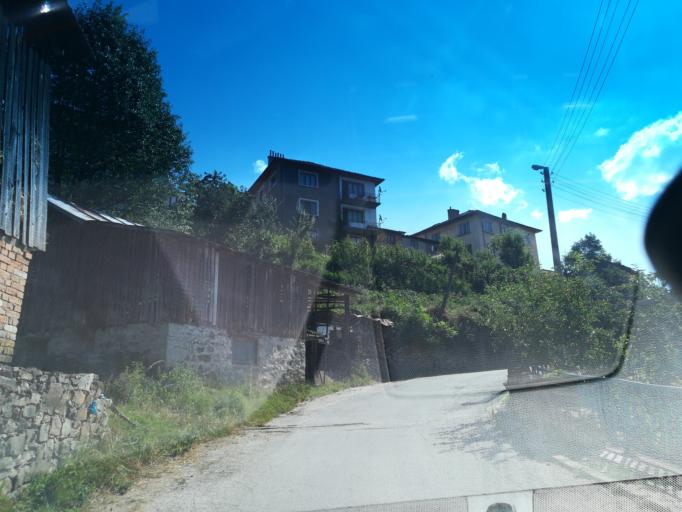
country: BG
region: Smolyan
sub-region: Obshtina Smolyan
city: Smolyan
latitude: 41.6584
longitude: 24.8305
